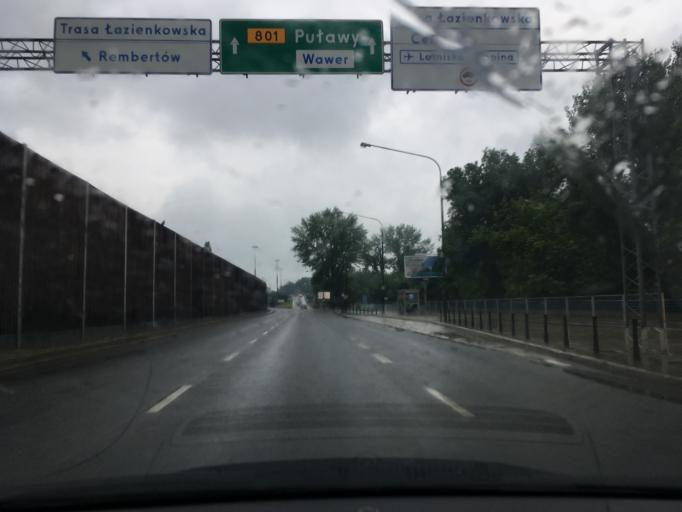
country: PL
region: Masovian Voivodeship
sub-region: Warszawa
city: Praga Polnoc
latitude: 52.2297
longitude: 21.0510
